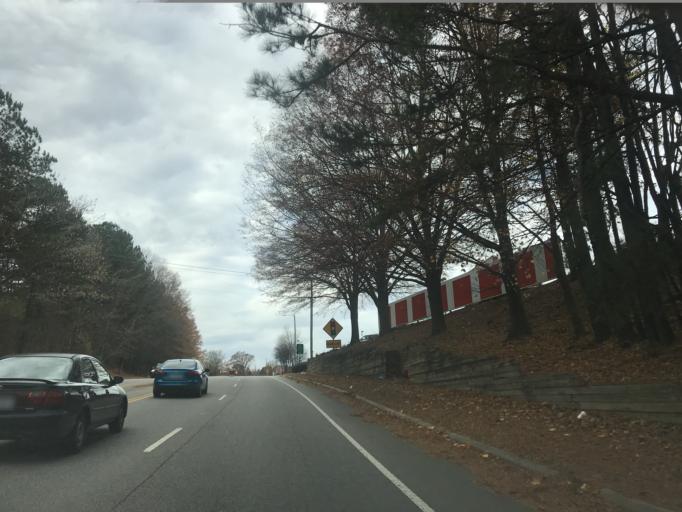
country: US
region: North Carolina
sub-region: Wake County
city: Raleigh
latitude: 35.8600
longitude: -78.5977
